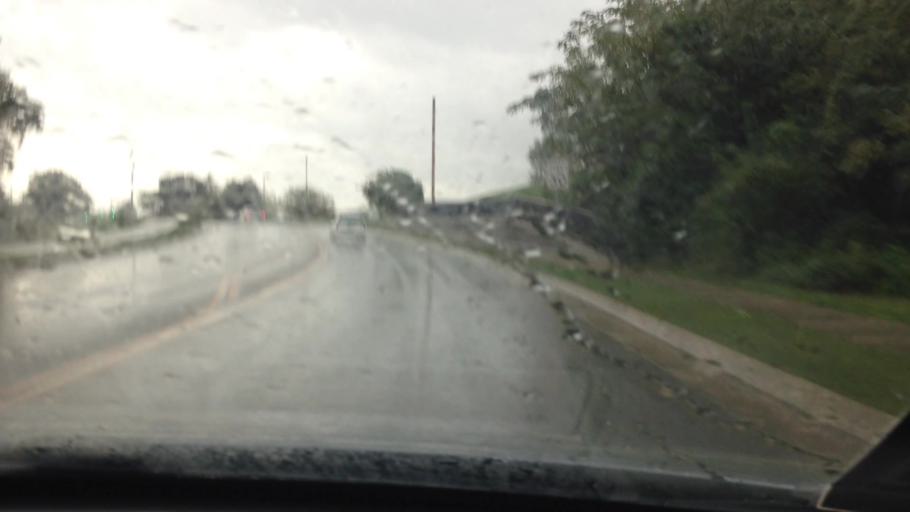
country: US
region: Kansas
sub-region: Leavenworth County
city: Leavenworth
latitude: 39.2888
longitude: -94.9127
